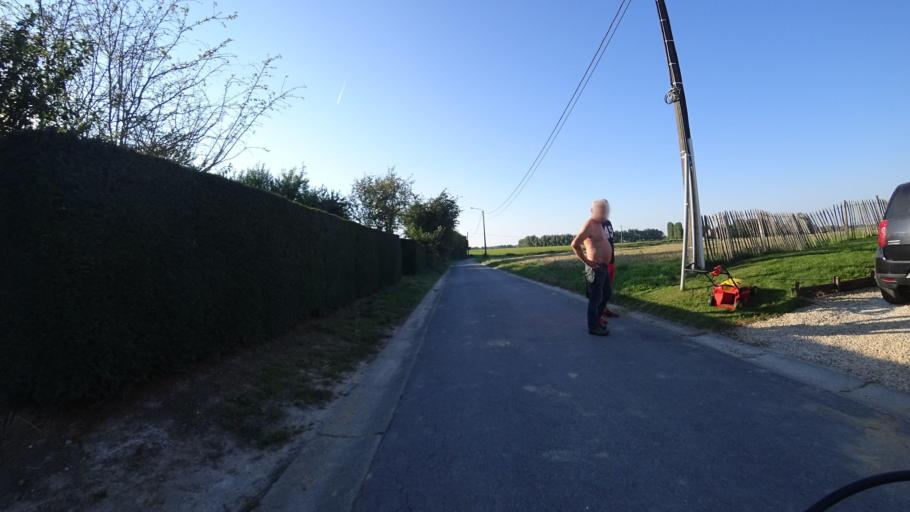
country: BE
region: Wallonia
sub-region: Province du Brabant Wallon
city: Perwez
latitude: 50.5867
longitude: 4.7682
